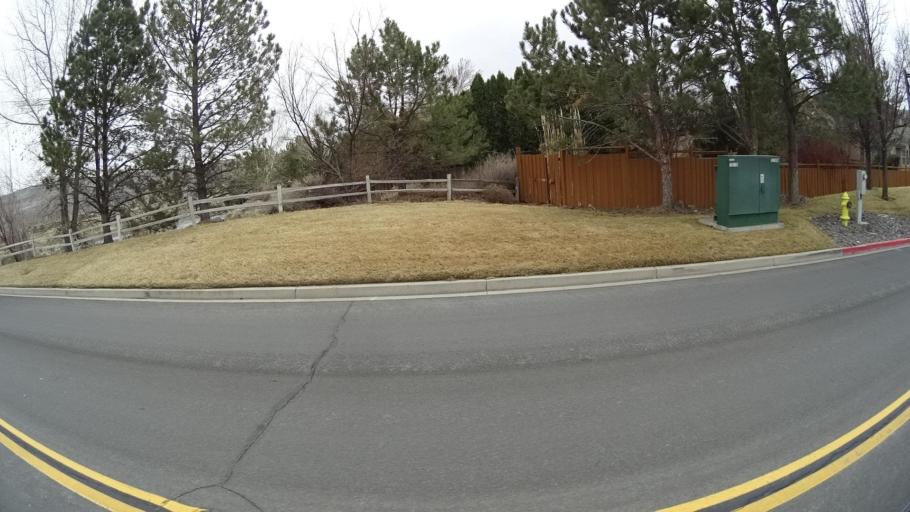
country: US
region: Nevada
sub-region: Washoe County
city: Spanish Springs
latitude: 39.6145
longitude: -119.6824
